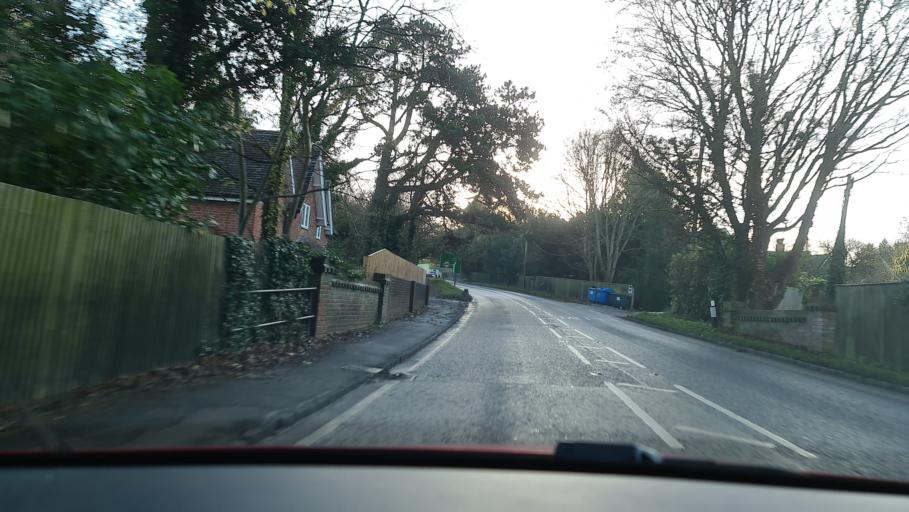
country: GB
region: England
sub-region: Buckinghamshire
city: Princes Risborough
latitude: 51.7515
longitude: -0.8076
